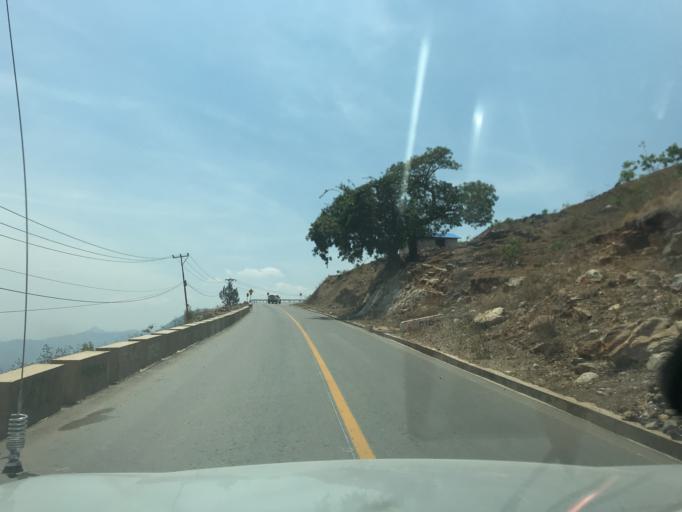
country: TL
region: Aileu
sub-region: Aileu Villa
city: Aileu
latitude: -8.8036
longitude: 125.5899
